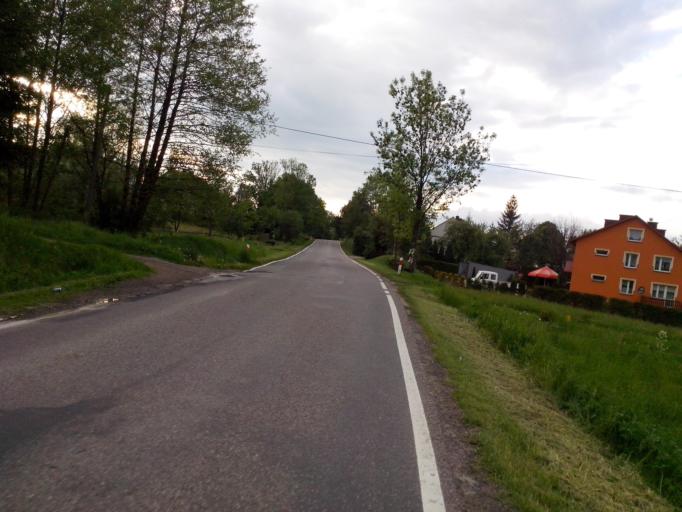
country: PL
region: Subcarpathian Voivodeship
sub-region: Powiat strzyzowski
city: Strzyzow
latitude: 49.8237
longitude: 21.8316
